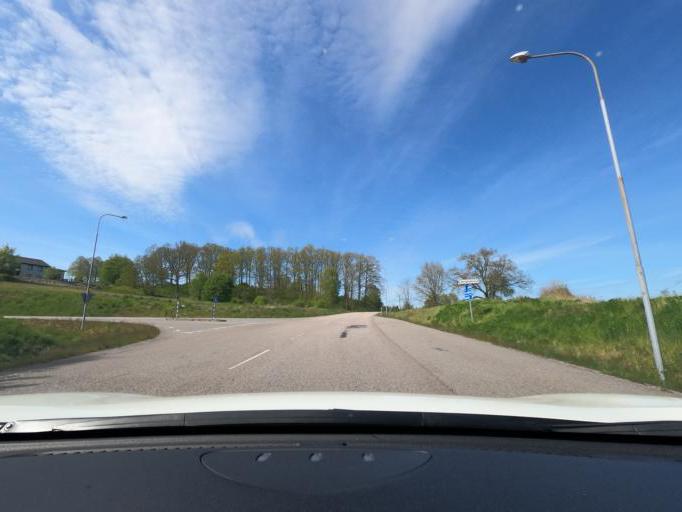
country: SE
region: Vaestra Goetaland
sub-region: Marks Kommun
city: Kinna
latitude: 57.4644
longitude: 12.5931
